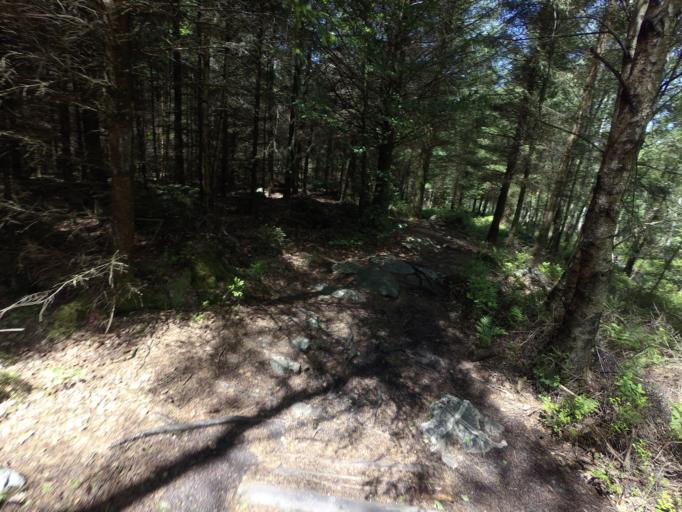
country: BE
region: Wallonia
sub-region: Province de Liege
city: Jalhay
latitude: 50.5189
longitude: 6.0016
